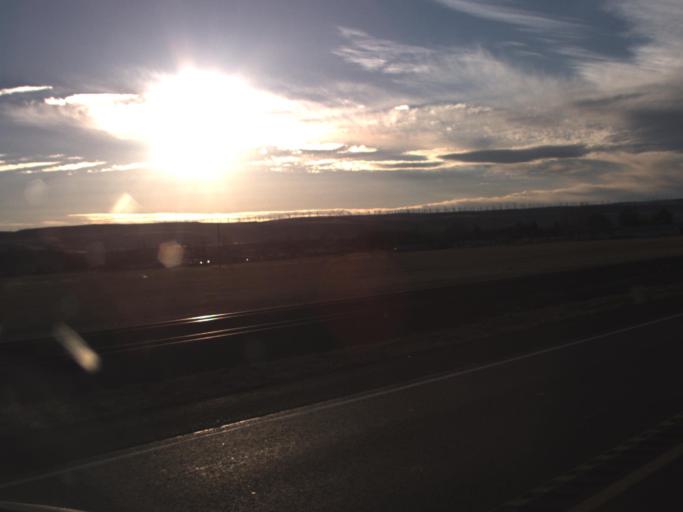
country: US
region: Washington
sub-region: Walla Walla County
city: Garrett
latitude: 46.0395
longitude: -118.6617
